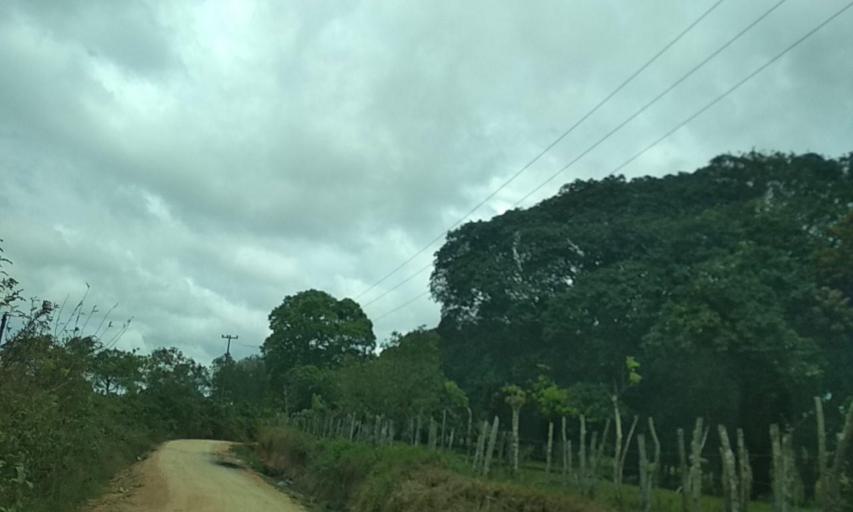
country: MX
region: Veracruz
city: Las Choapas
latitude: 17.8913
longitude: -94.1190
